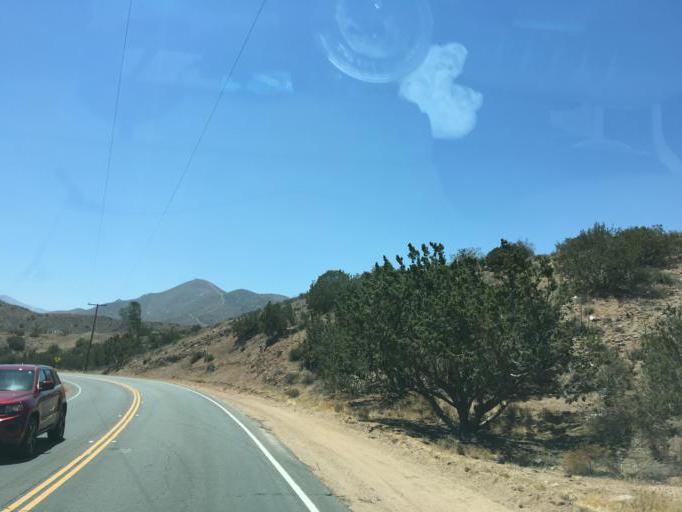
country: US
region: California
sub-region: Los Angeles County
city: Acton
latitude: 34.4852
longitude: -118.2141
